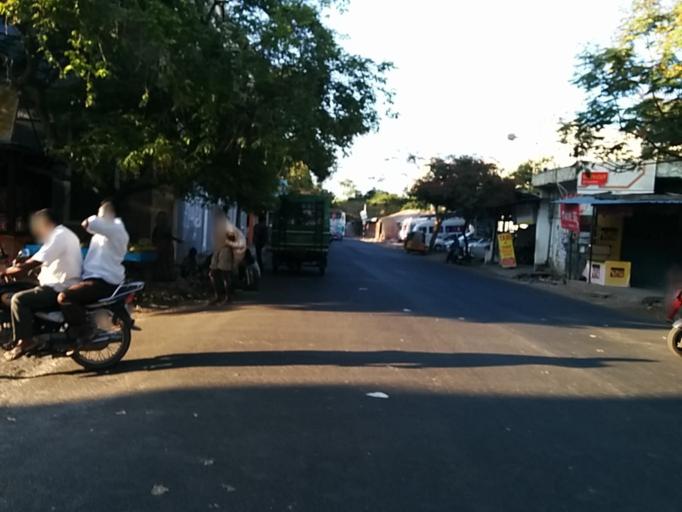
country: IN
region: Pondicherry
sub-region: Puducherry
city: Puducherry
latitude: 11.9326
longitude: 79.8321
